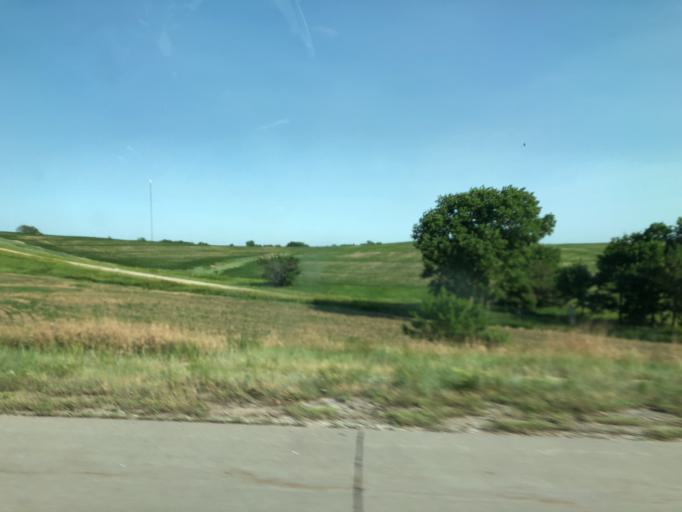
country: US
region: Nebraska
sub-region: Sarpy County
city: Gretna
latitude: 41.0892
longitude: -96.2638
